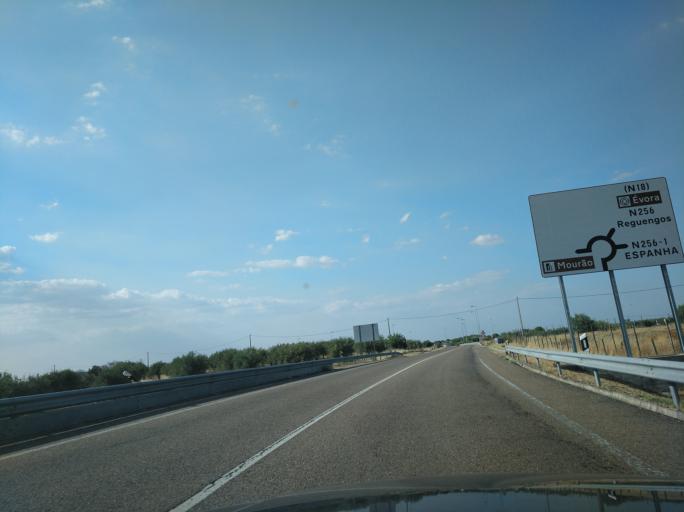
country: PT
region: Evora
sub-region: Mourao
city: Mourao
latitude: 38.3797
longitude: -7.3316
